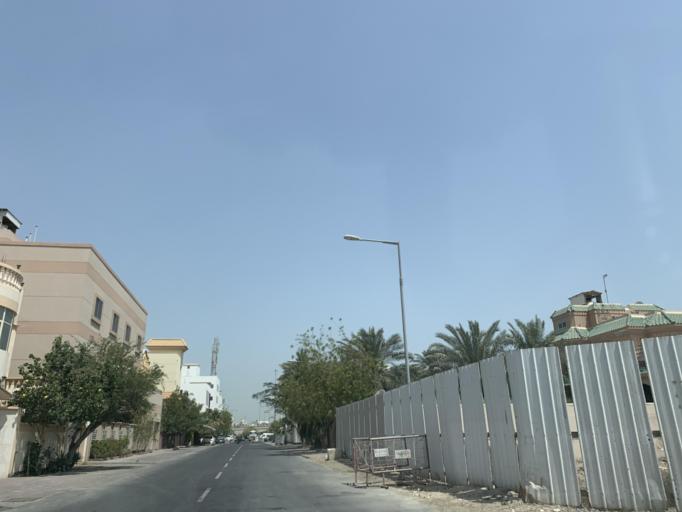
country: BH
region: Manama
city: Manama
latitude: 26.2011
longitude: 50.5655
